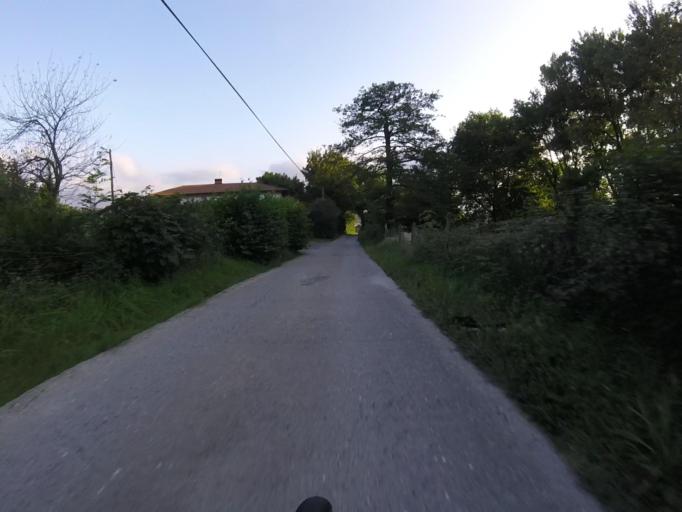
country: ES
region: Basque Country
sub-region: Provincia de Guipuzcoa
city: Lezo
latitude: 43.3315
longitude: -1.8620
